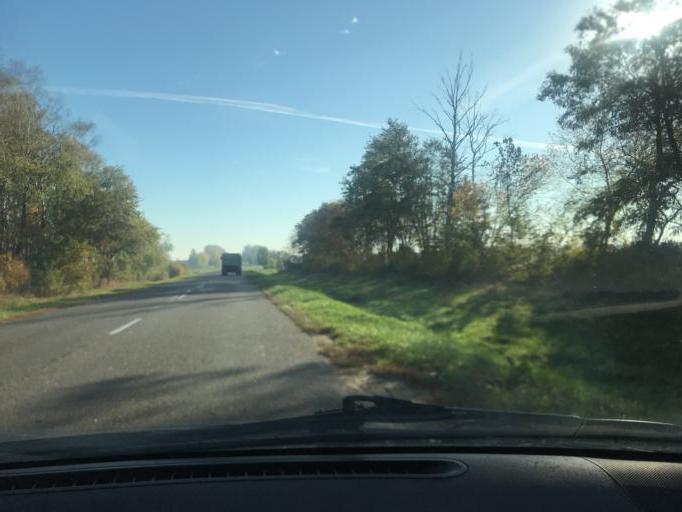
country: BY
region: Brest
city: Ivanava
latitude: 52.1450
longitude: 25.4838
